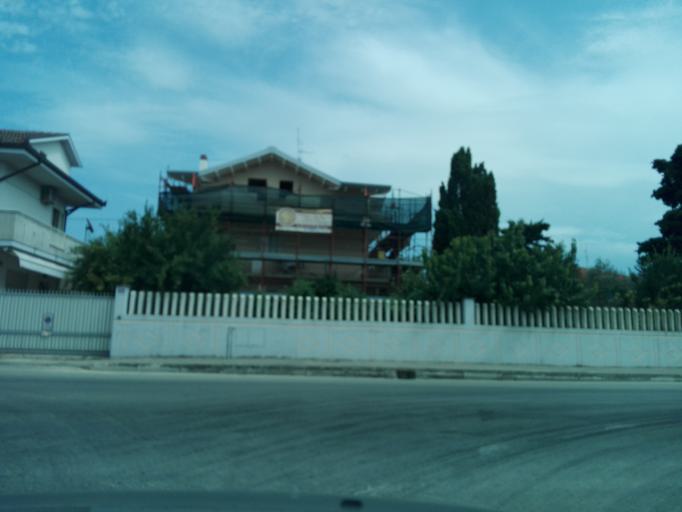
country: IT
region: Abruzzo
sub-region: Provincia di Pescara
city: Cappelle sul Tavo
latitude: 42.4831
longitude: 14.1164
